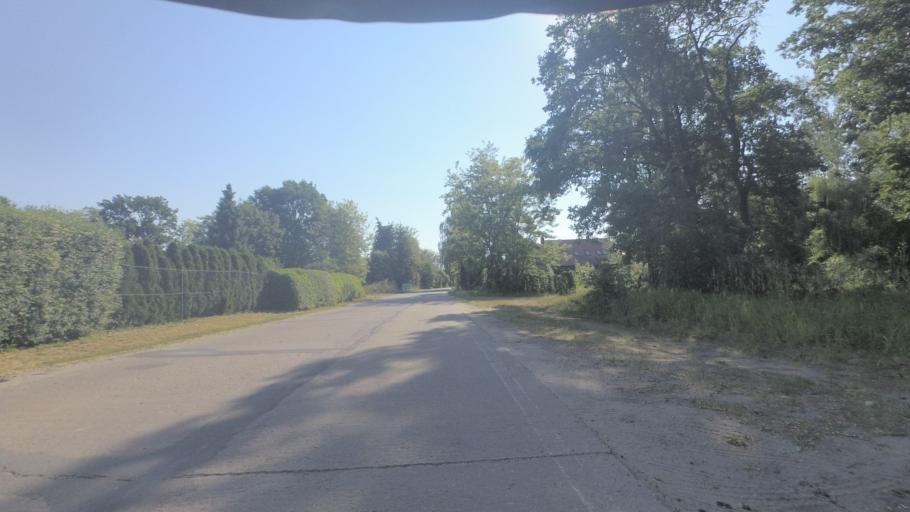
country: DE
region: Saxony-Anhalt
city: Quellendorf
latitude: 51.8162
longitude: 12.1425
